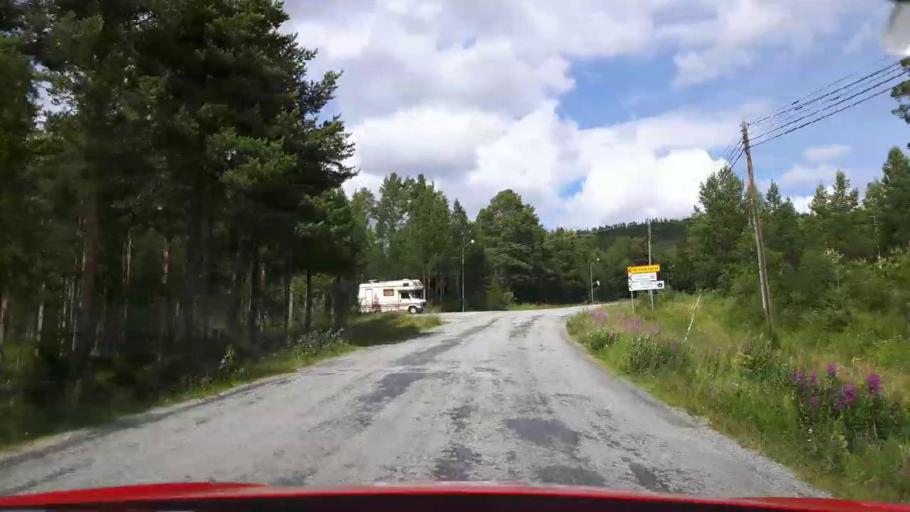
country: NO
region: Hedmark
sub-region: Engerdal
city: Engerdal
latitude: 62.4367
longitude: 12.6782
